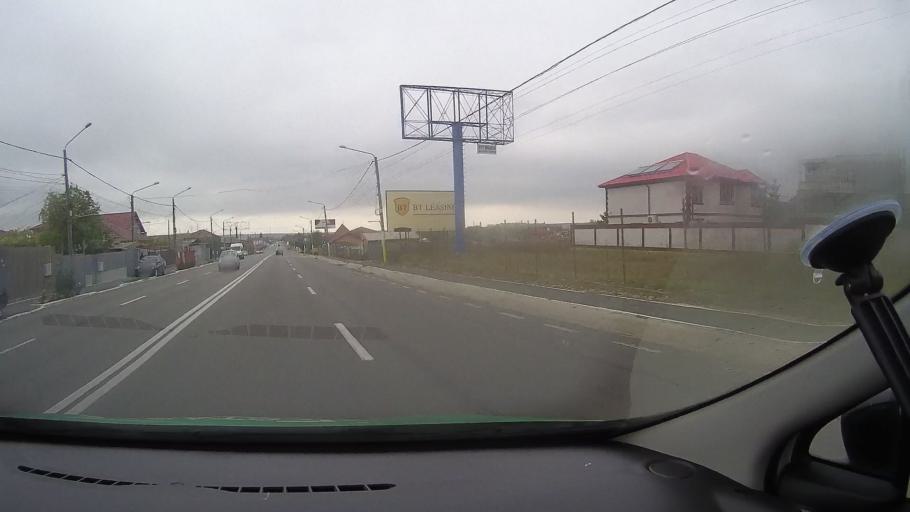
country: RO
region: Constanta
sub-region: Comuna Valu lui Traian
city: Valu lui Traian
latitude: 44.1683
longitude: 28.4483
